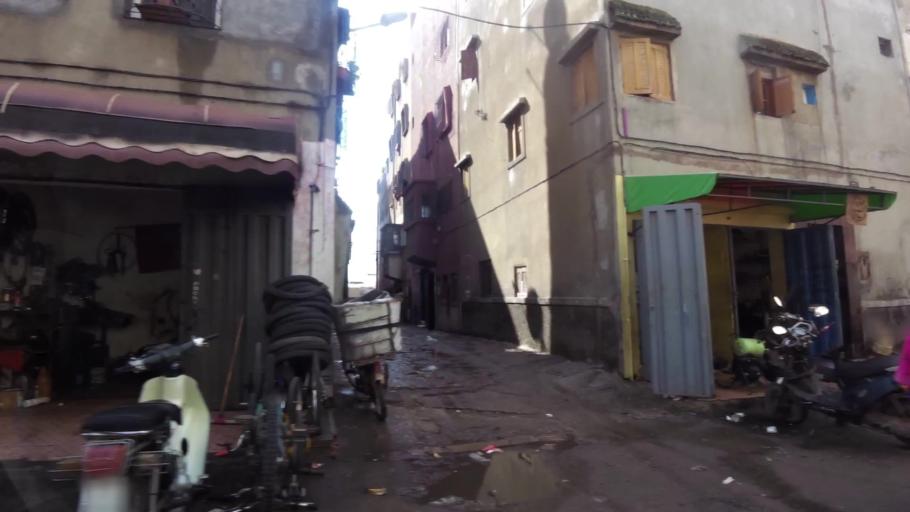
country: MA
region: Grand Casablanca
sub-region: Casablanca
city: Casablanca
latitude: 33.5324
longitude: -7.6688
